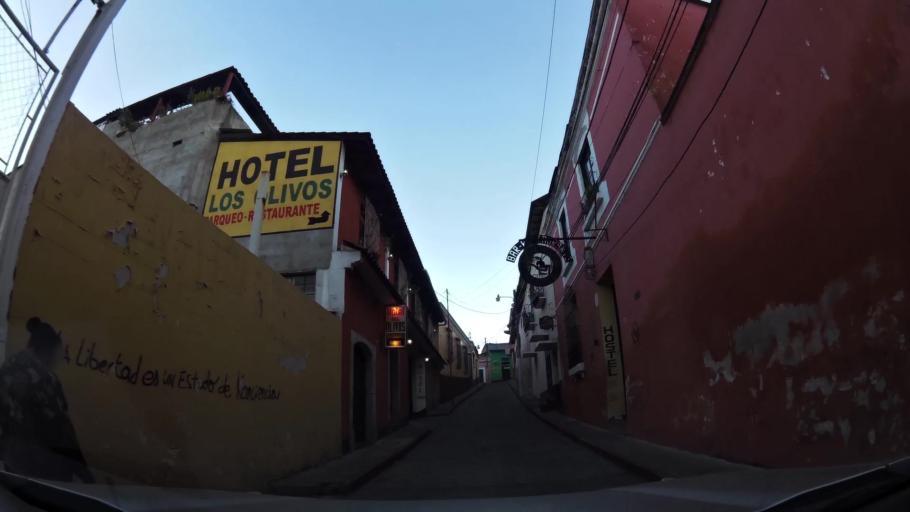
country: GT
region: Quetzaltenango
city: Quetzaltenango
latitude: 14.8357
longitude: -91.5189
